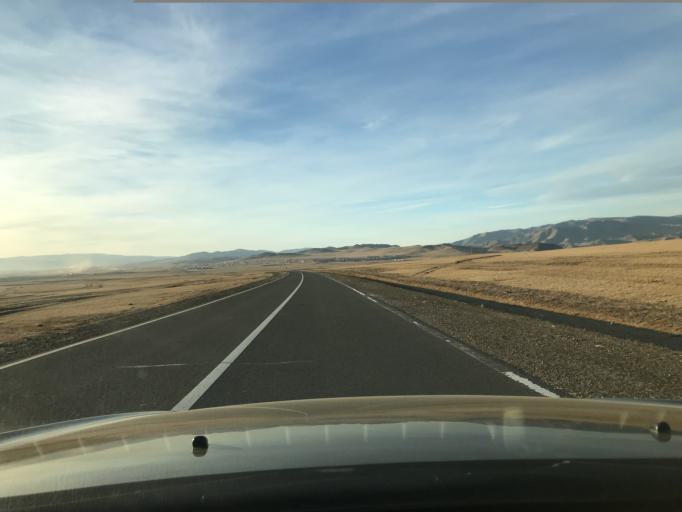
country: MN
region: Central Aimak
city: Arhust
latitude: 47.7624
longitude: 107.4365
